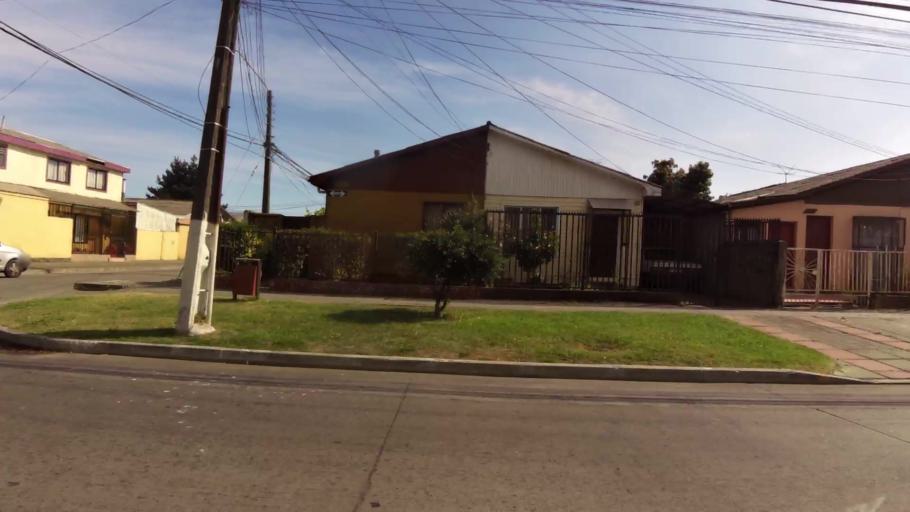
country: CL
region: Biobio
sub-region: Provincia de Concepcion
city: Talcahuano
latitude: -36.7867
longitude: -73.1033
